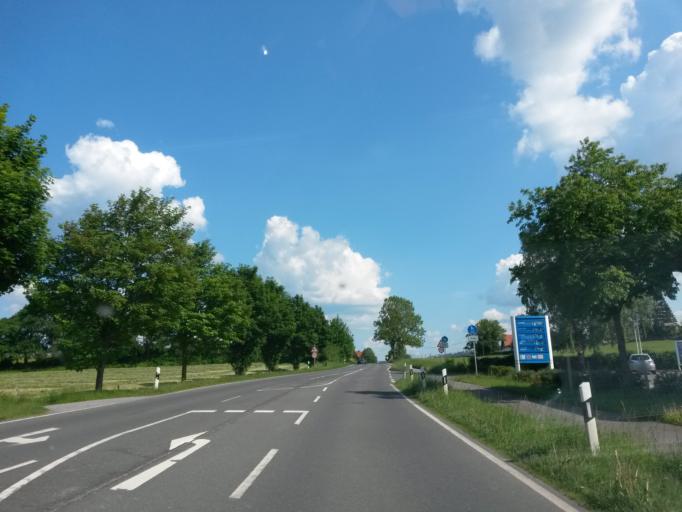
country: DE
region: North Rhine-Westphalia
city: Balve
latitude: 51.3150
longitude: 7.8751
